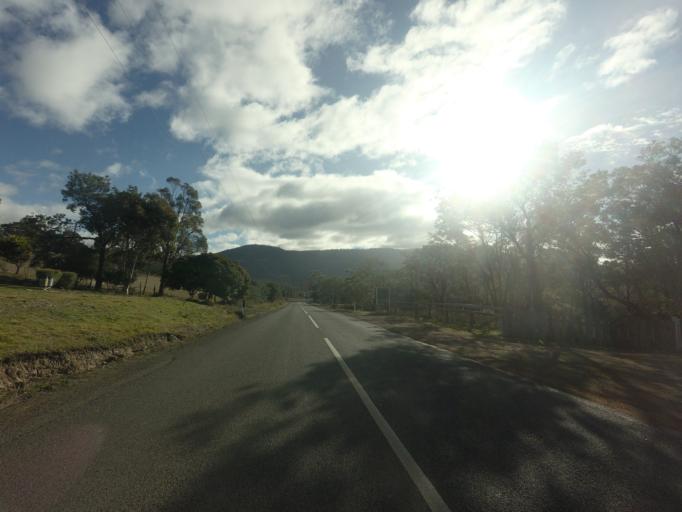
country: AU
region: Tasmania
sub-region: Derwent Valley
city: New Norfolk
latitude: -42.7857
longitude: 147.1182
